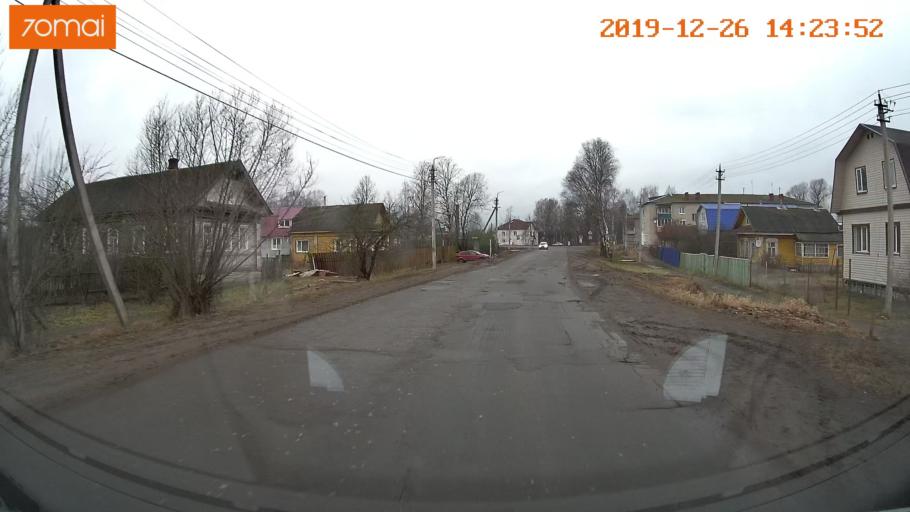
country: RU
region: Jaroslavl
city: Poshekhon'ye
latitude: 58.4983
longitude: 39.1118
